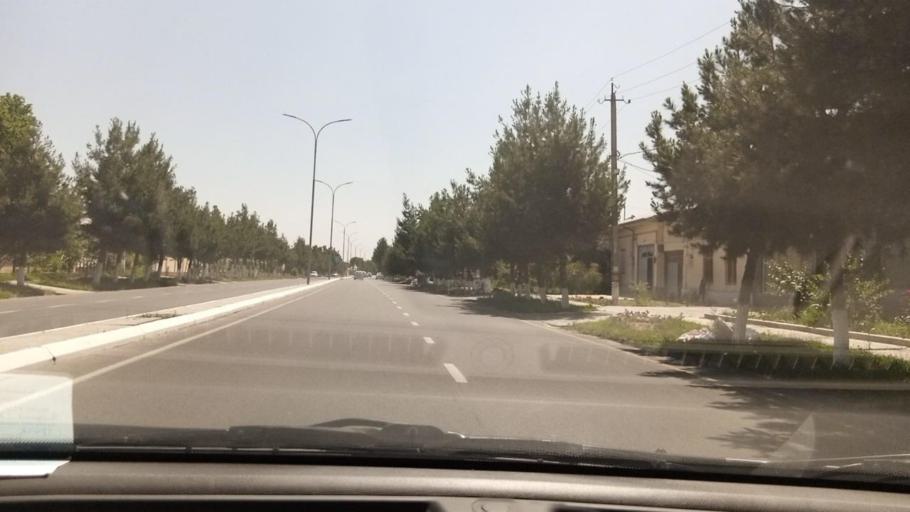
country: UZ
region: Toshkent
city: Urtaowul
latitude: 41.2137
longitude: 69.1722
